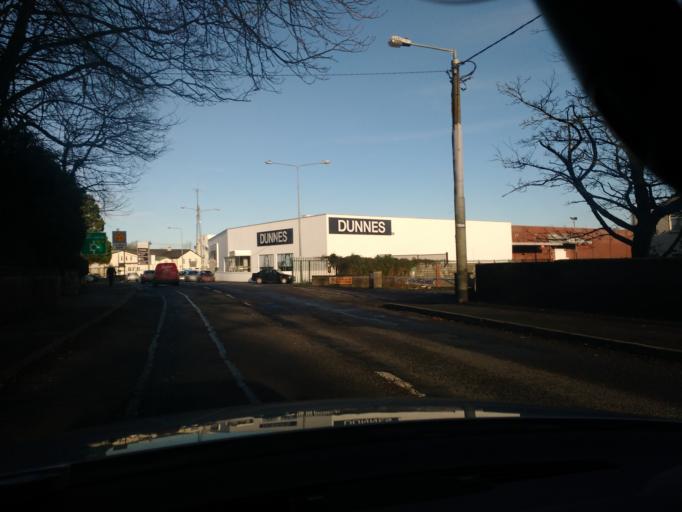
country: IE
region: Munster
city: Thurles
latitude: 52.6741
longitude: -7.8124
